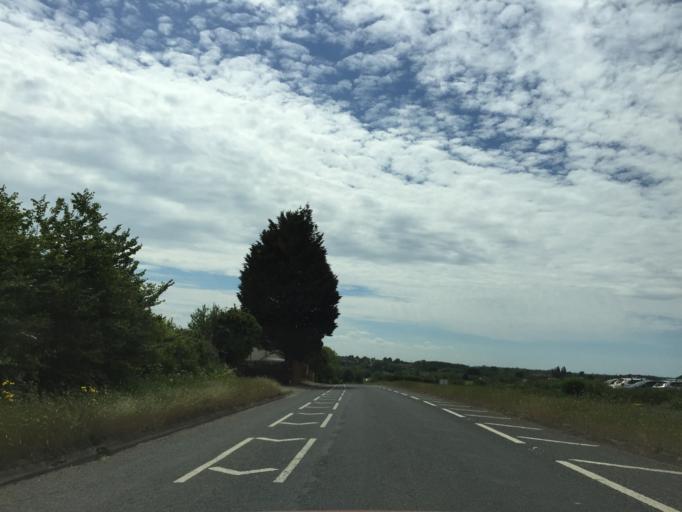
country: GB
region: England
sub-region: Gloucestershire
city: Stonehouse
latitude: 51.7689
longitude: -2.3269
